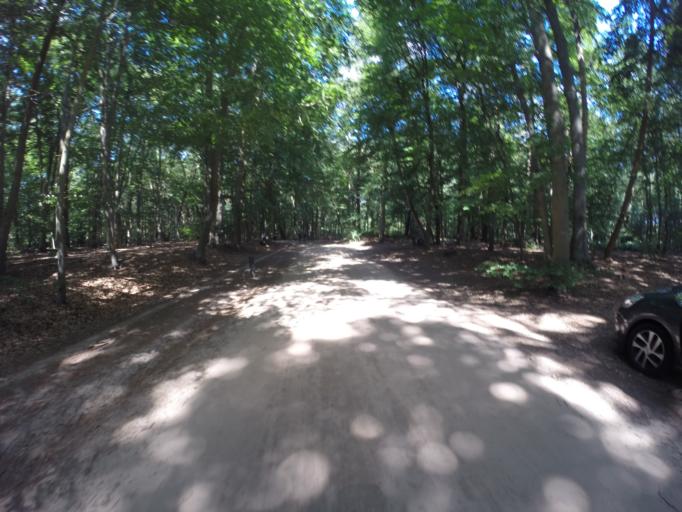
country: NL
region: Gelderland
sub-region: Gemeente Lochem
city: Barchem
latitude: 52.0993
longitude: 6.4549
